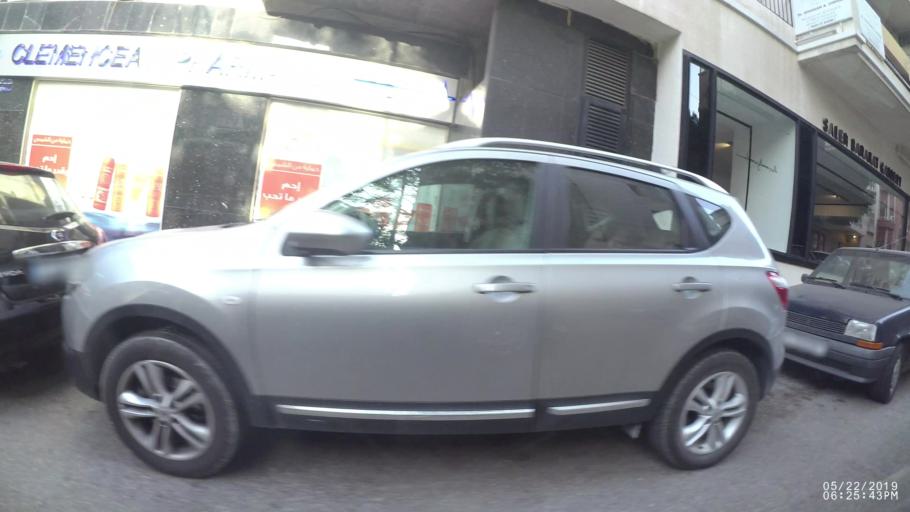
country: LB
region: Beyrouth
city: Ra's Bayrut
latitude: 33.8978
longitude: 35.4914
